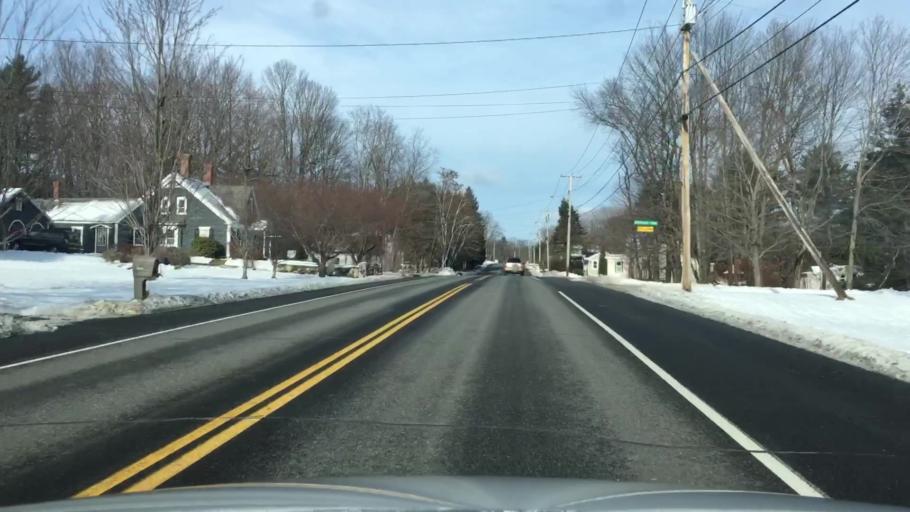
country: US
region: Maine
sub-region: Androscoggin County
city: Lewiston
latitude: 44.1453
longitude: -70.1918
